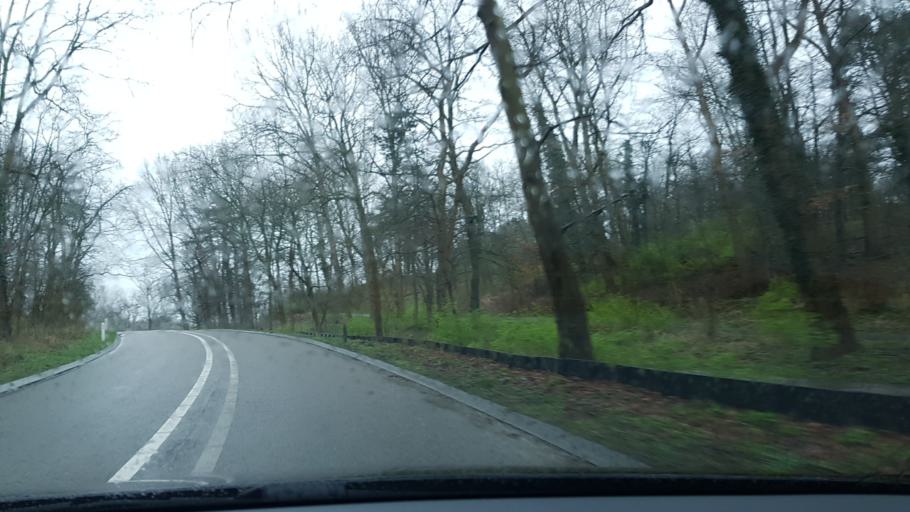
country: NL
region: North Holland
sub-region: Gemeente Bloemendaal
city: Bloemendaal
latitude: 52.3907
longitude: 4.5973
